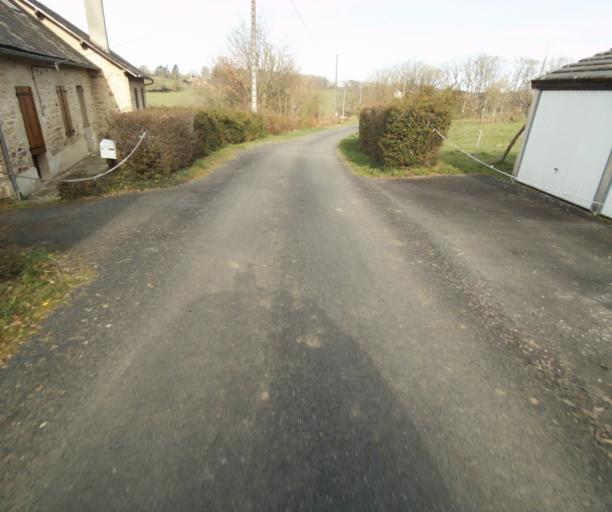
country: FR
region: Limousin
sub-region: Departement de la Correze
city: Chamboulive
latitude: 45.4212
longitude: 1.7623
